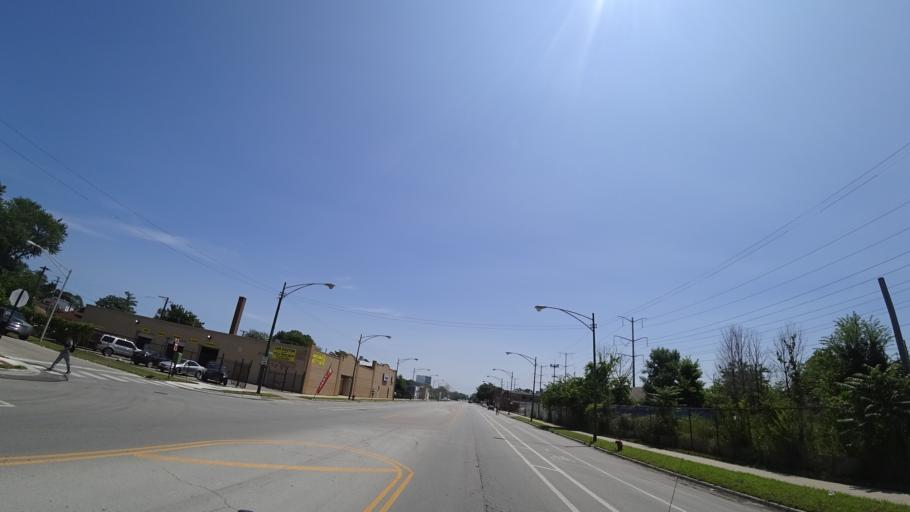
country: US
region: Indiana
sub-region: Lake County
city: Whiting
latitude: 41.7432
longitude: -87.5741
